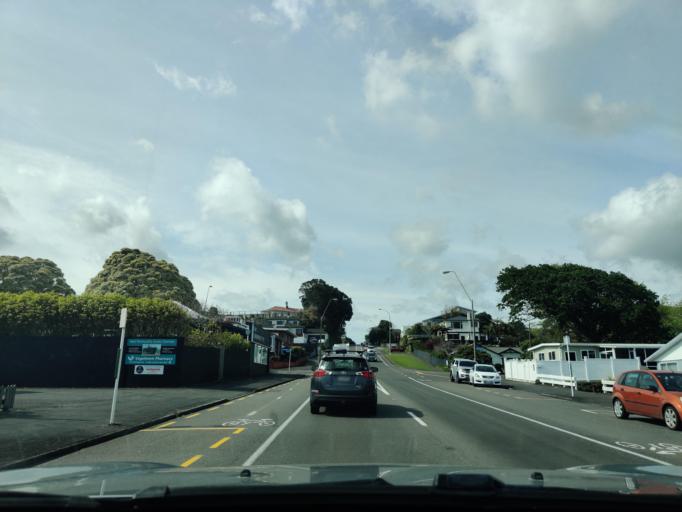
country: NZ
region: Taranaki
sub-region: New Plymouth District
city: New Plymouth
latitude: -39.0580
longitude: 174.0842
